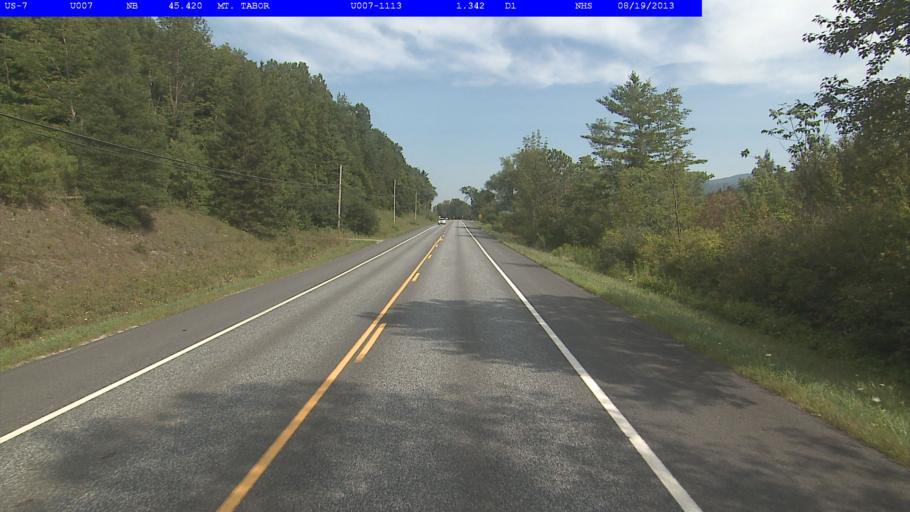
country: US
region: Vermont
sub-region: Bennington County
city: Manchester Center
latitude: 43.3242
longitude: -72.9912
